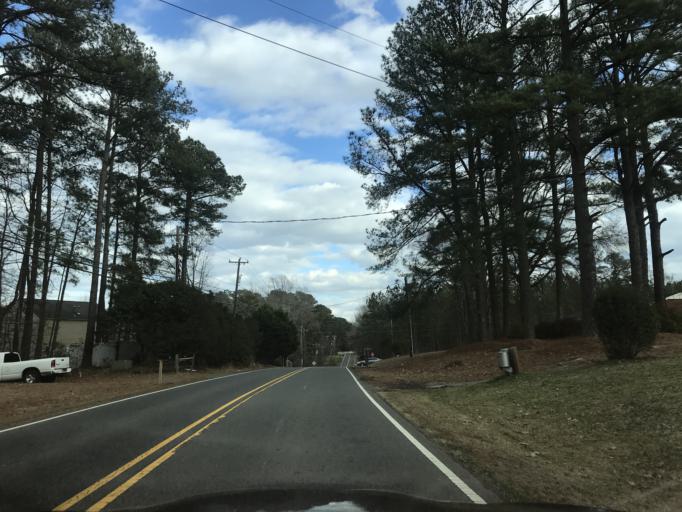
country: US
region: North Carolina
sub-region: Durham County
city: Durham
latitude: 35.9682
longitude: -78.8395
